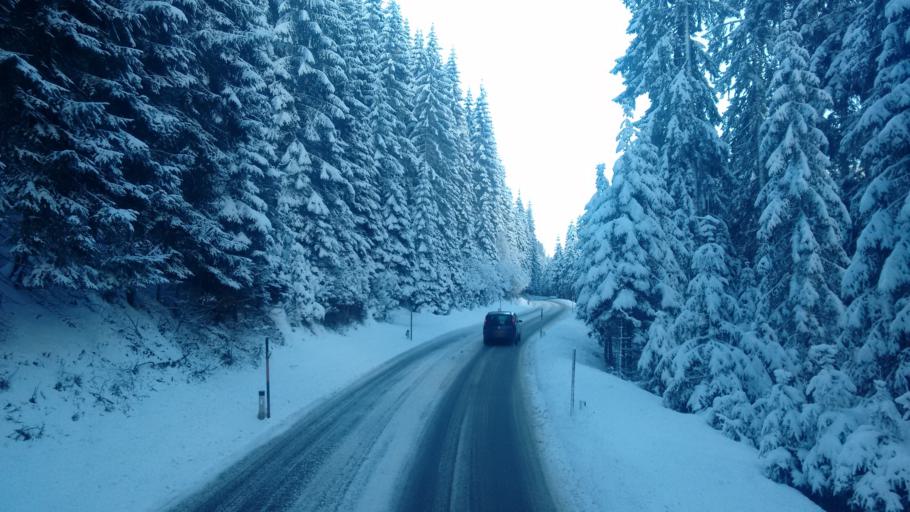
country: AT
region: Salzburg
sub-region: Politischer Bezirk Sankt Johann im Pongau
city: Flachau
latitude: 47.3236
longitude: 13.4453
